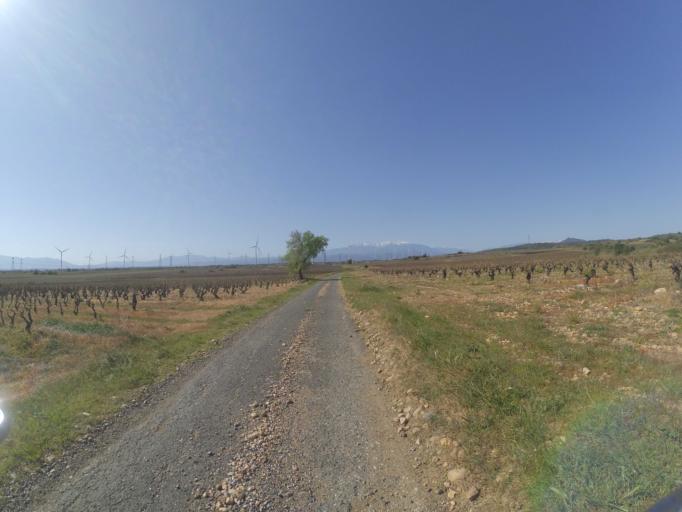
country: FR
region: Languedoc-Roussillon
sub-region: Departement des Pyrenees-Orientales
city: Baixas
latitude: 42.7393
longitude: 2.7942
